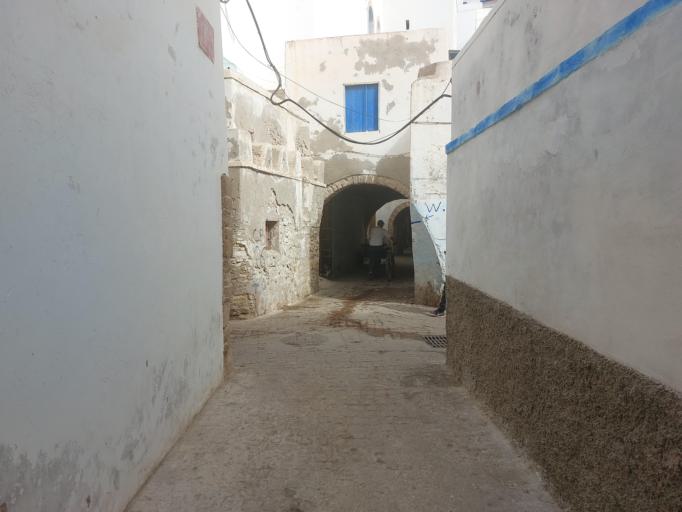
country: MA
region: Marrakech-Tensift-Al Haouz
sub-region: Essaouira
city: Essaouira
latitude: 31.5126
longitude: -9.7681
